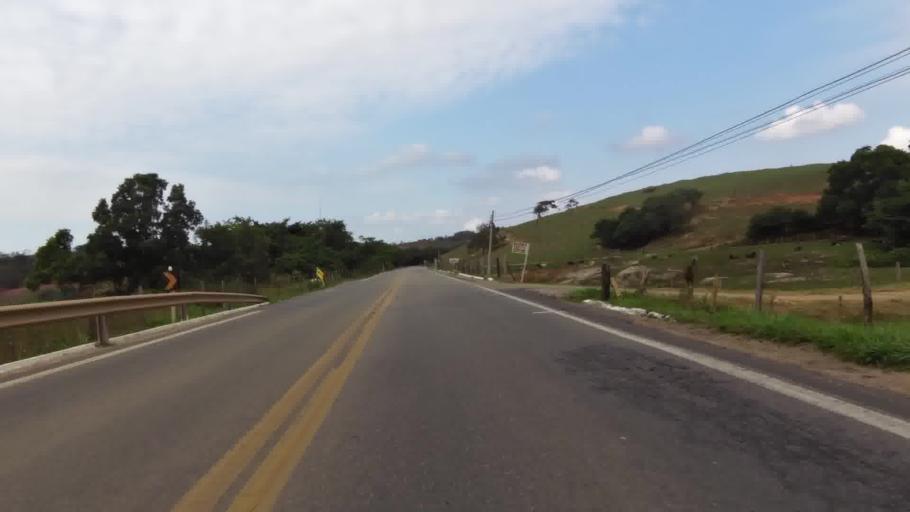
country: BR
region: Espirito Santo
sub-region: Piuma
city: Piuma
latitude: -20.8745
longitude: -40.7623
